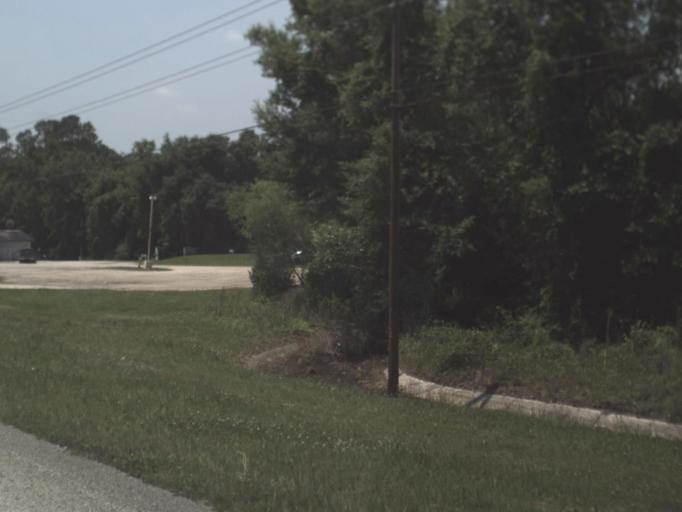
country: US
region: Florida
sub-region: Duval County
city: Baldwin
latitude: 30.1953
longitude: -82.0172
